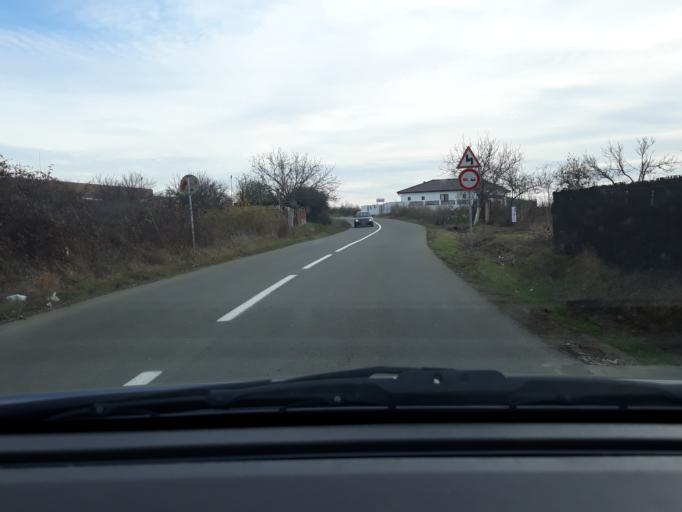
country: RO
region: Bihor
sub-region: Comuna Sanmartin
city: Sanmartin
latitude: 47.0298
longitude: 21.9984
